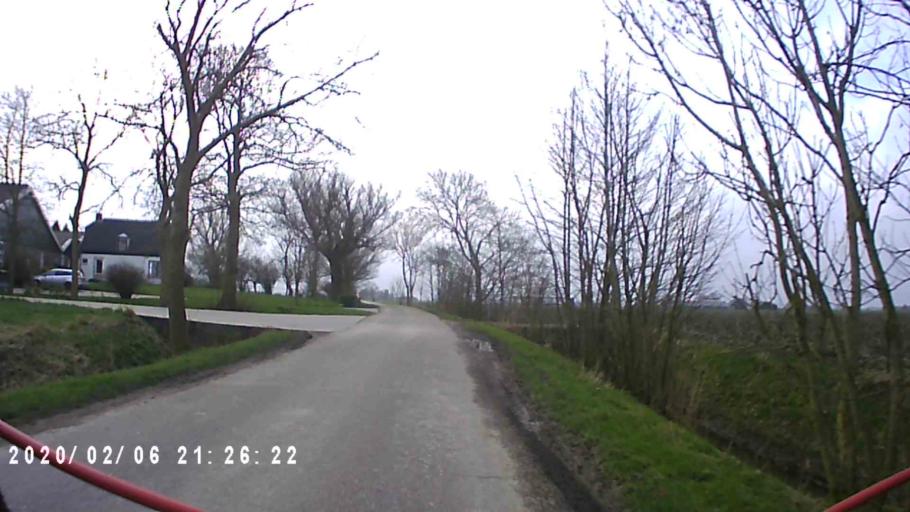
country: NL
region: Groningen
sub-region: Gemeente Zuidhorn
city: Oldehove
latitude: 53.2880
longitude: 6.3778
